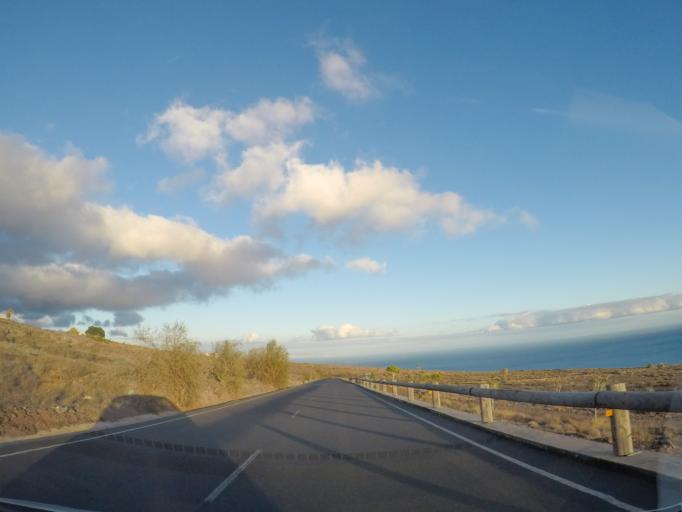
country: ES
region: Canary Islands
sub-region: Provincia de Santa Cruz de Tenerife
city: Alajero
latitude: 28.0373
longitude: -17.2232
